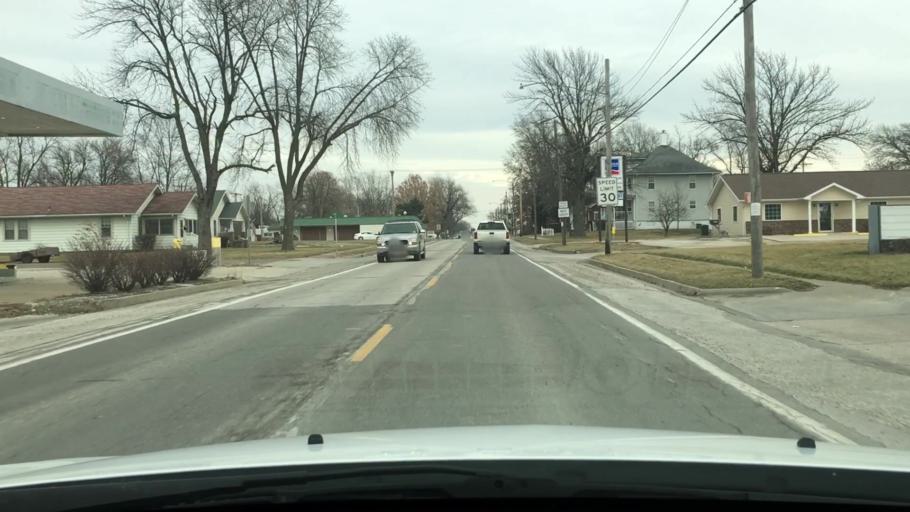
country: US
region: Missouri
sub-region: Audrain County
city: Vandalia
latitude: 39.3082
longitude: -91.4943
